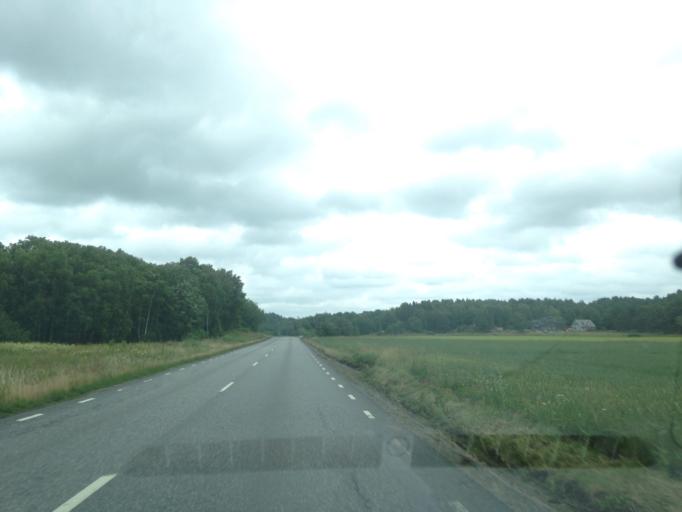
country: SE
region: Vaestra Goetaland
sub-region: Kungalvs Kommun
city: Kode
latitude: 57.8564
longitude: 11.8339
